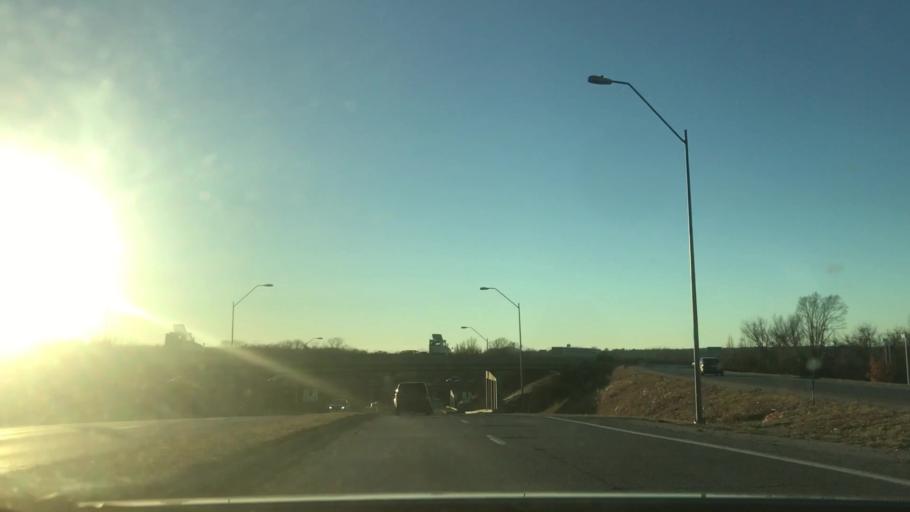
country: US
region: Missouri
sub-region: Platte County
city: Riverside
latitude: 39.1807
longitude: -94.5844
